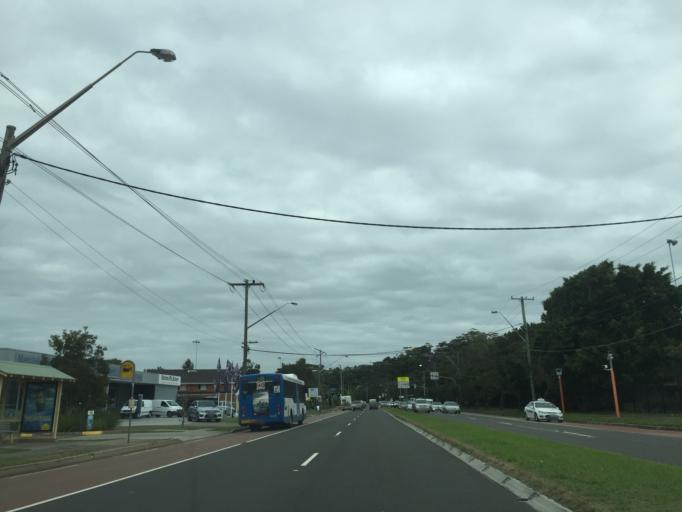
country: AU
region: New South Wales
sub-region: Pittwater
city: North Narrabeen
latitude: -33.7006
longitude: 151.2995
